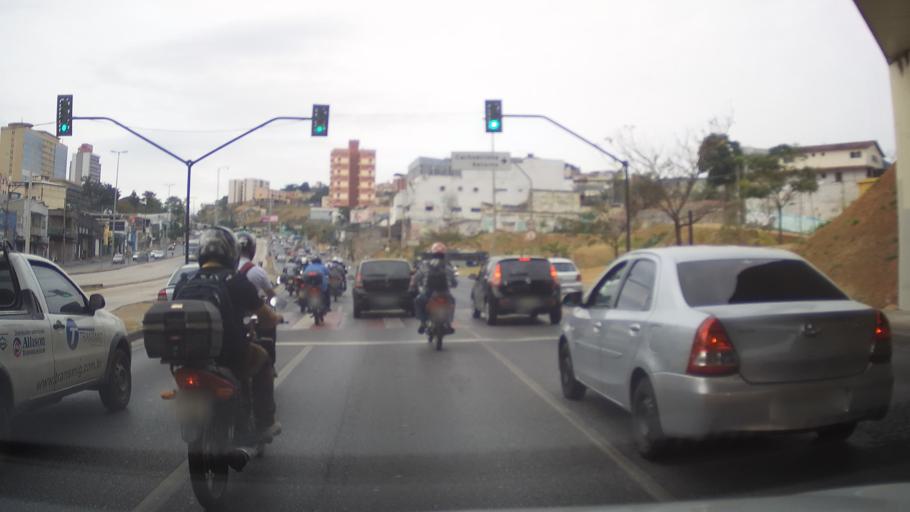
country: BR
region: Minas Gerais
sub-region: Belo Horizonte
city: Belo Horizonte
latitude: -19.8931
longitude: -43.9503
